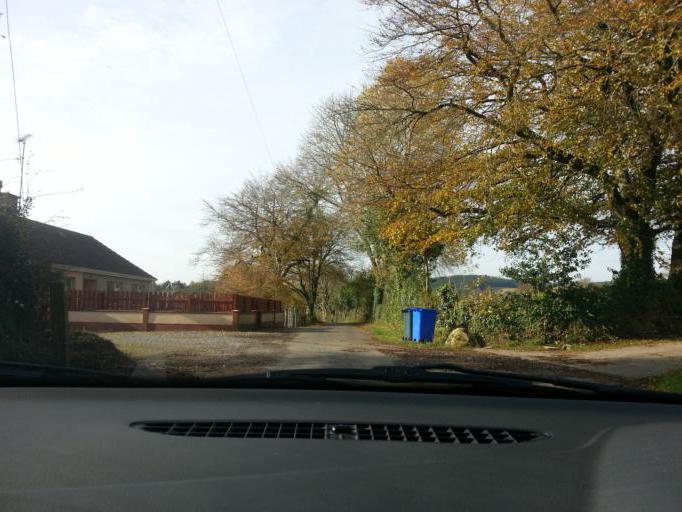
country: IE
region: Ulster
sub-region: County Monaghan
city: Clones
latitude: 54.2312
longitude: -7.2940
